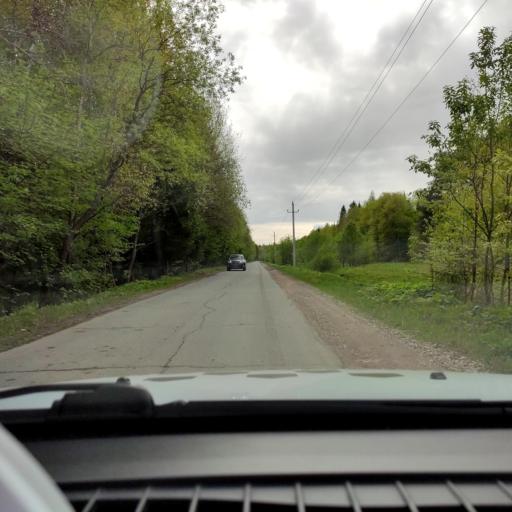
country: RU
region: Perm
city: Novyye Lyady
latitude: 58.0434
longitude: 56.6336
